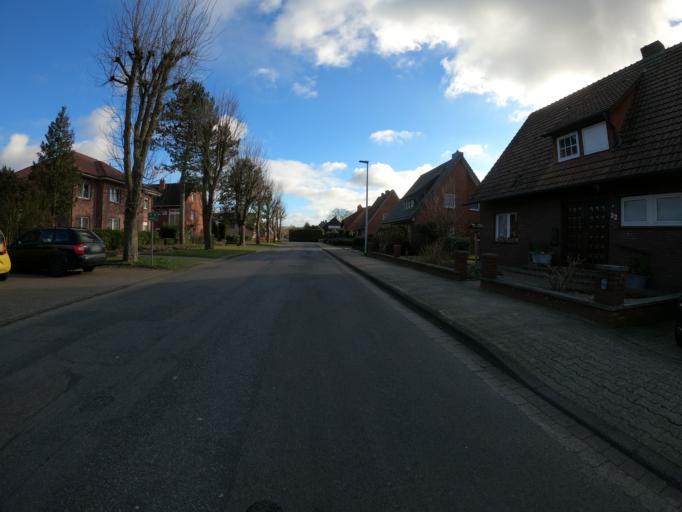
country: DE
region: Lower Saxony
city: Haselunne
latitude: 52.6727
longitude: 7.4759
